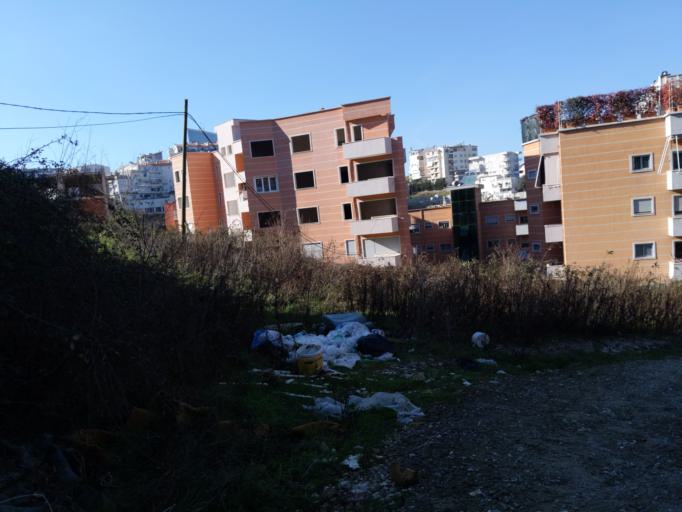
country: AL
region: Tirane
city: Tirana
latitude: 41.3081
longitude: 19.8046
